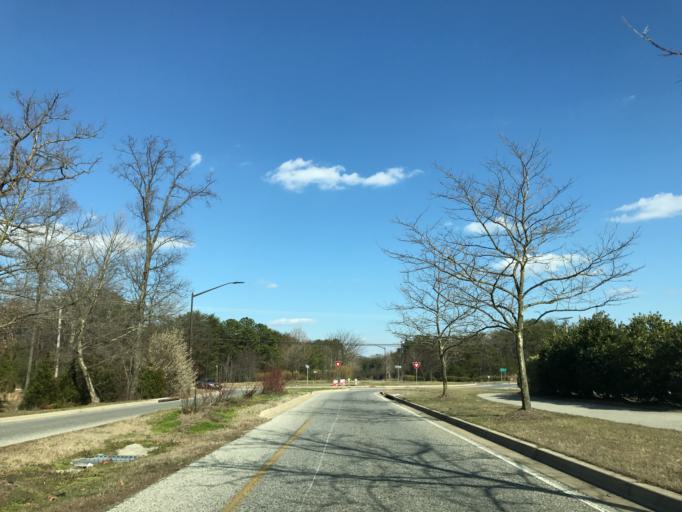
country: US
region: Maryland
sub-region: Anne Arundel County
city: Pasadena
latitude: 39.1075
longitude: -76.5842
